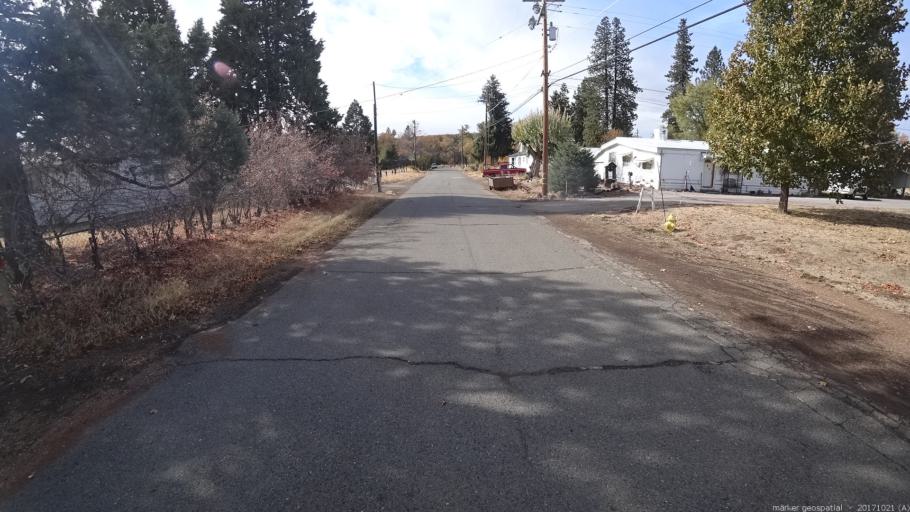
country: US
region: California
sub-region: Shasta County
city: Burney
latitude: 40.8845
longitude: -121.6654
